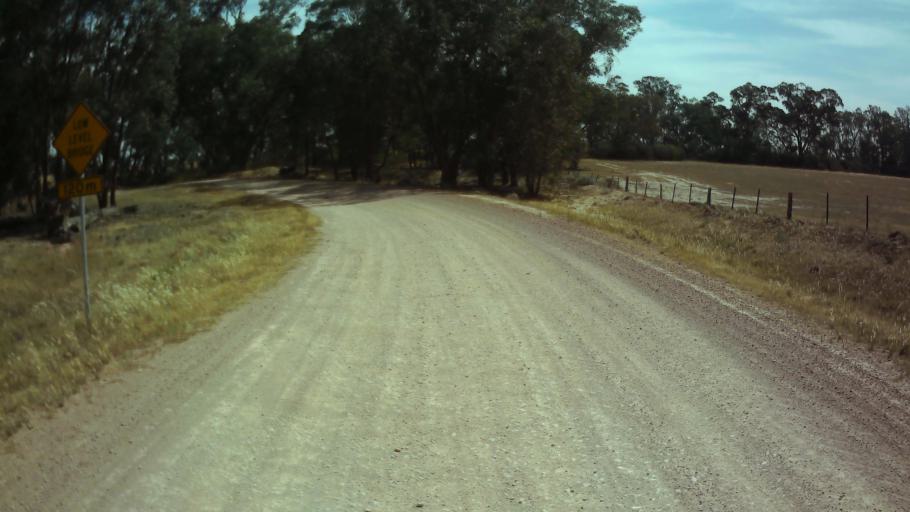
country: AU
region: New South Wales
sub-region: Weddin
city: Grenfell
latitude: -34.0406
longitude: 148.0799
